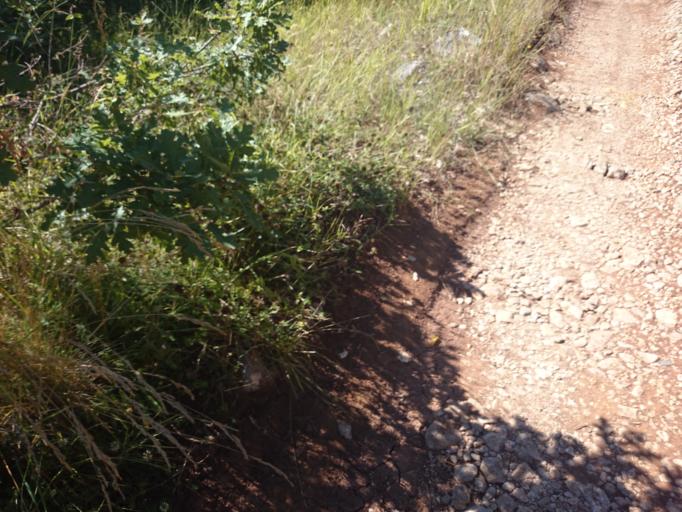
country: AL
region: Diber
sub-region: Rrethi i Bulqizes
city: Zerqan
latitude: 41.4775
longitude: 20.3679
